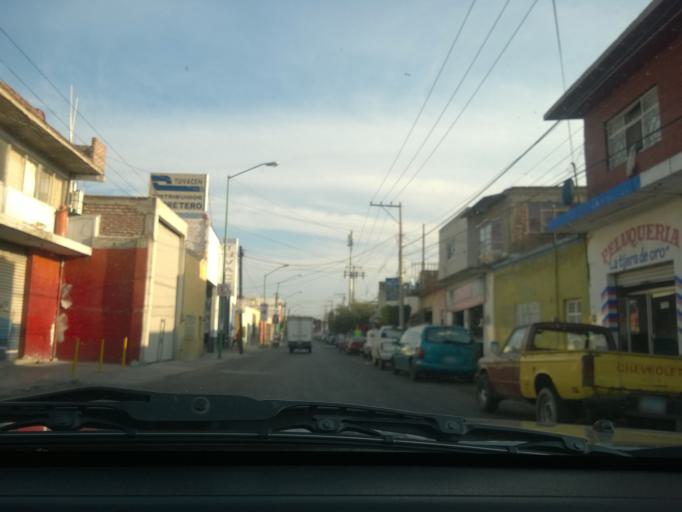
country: MX
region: Guanajuato
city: Leon
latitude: 21.1375
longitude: -101.6822
